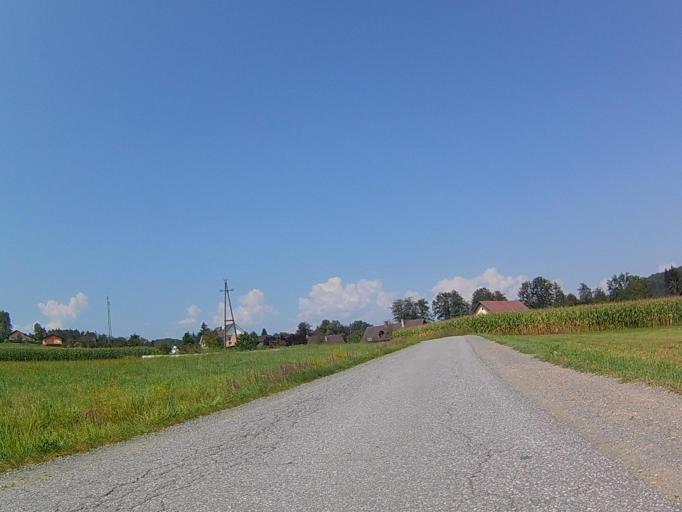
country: AT
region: Styria
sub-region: Politischer Bezirk Leibnitz
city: Oberhaag
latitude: 46.6889
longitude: 15.3257
